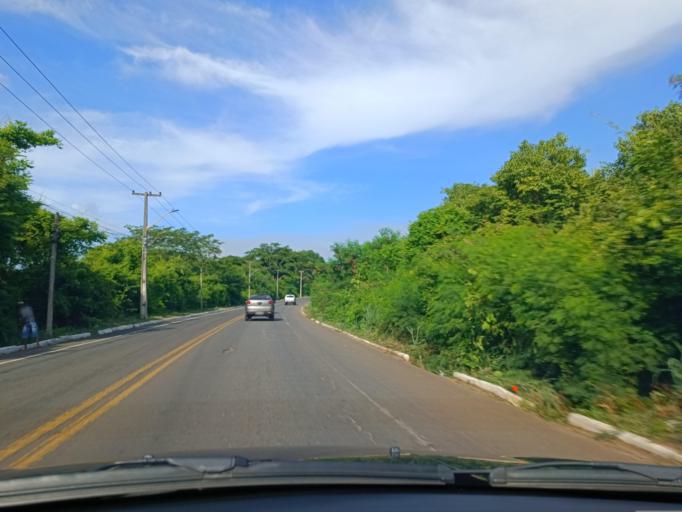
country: BR
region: Piaui
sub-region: Teresina
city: Teresina
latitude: -5.0850
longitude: -42.7555
